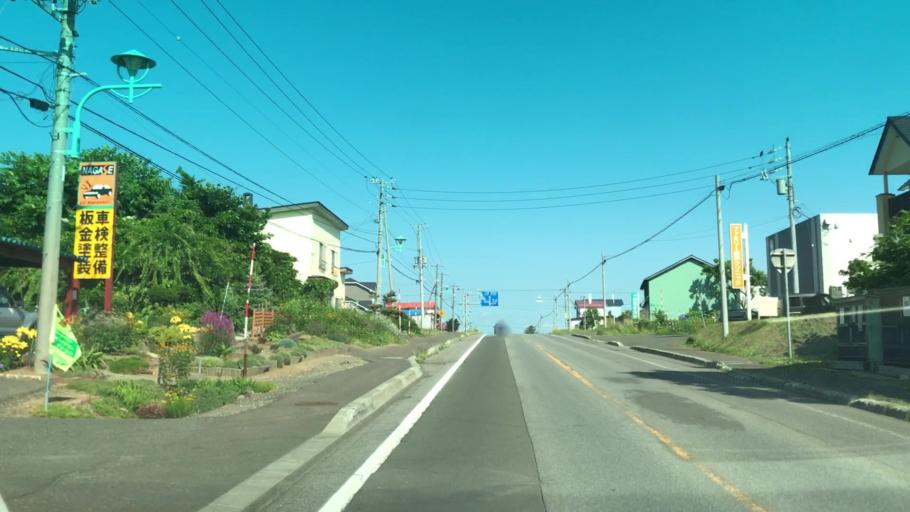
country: JP
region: Hokkaido
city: Iwanai
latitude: 42.9820
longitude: 140.5706
